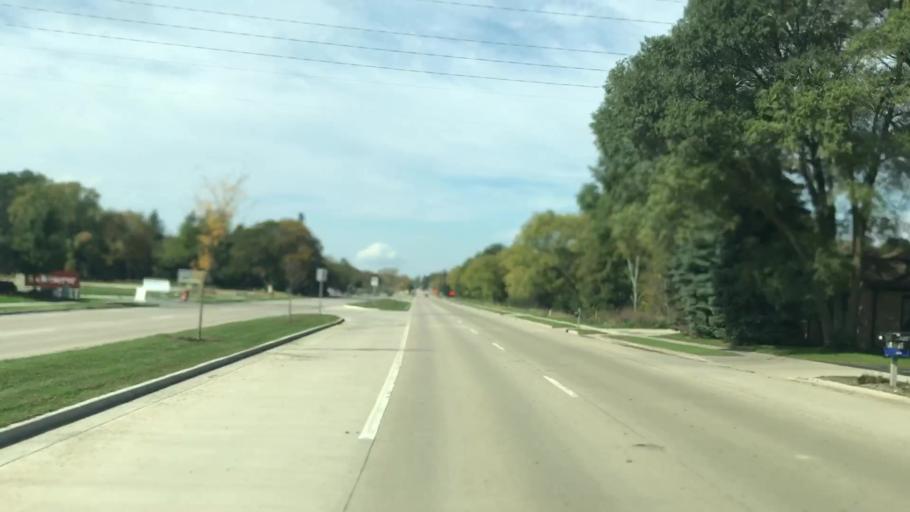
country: US
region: Wisconsin
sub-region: Ozaukee County
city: Mequon
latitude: 43.2217
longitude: -87.9931
